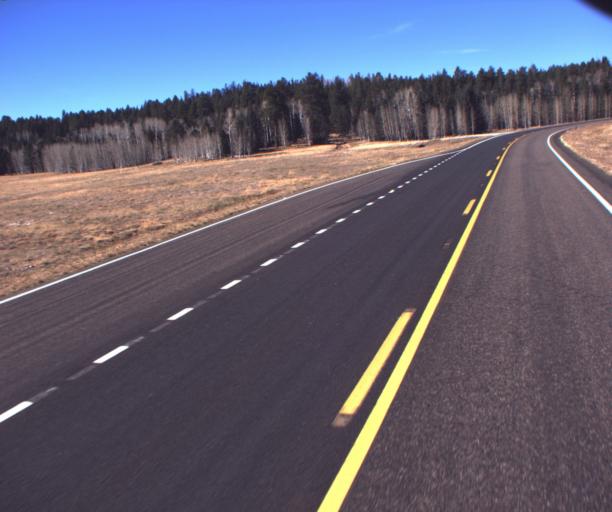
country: US
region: Arizona
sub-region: Coconino County
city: Grand Canyon
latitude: 36.5032
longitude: -112.1396
